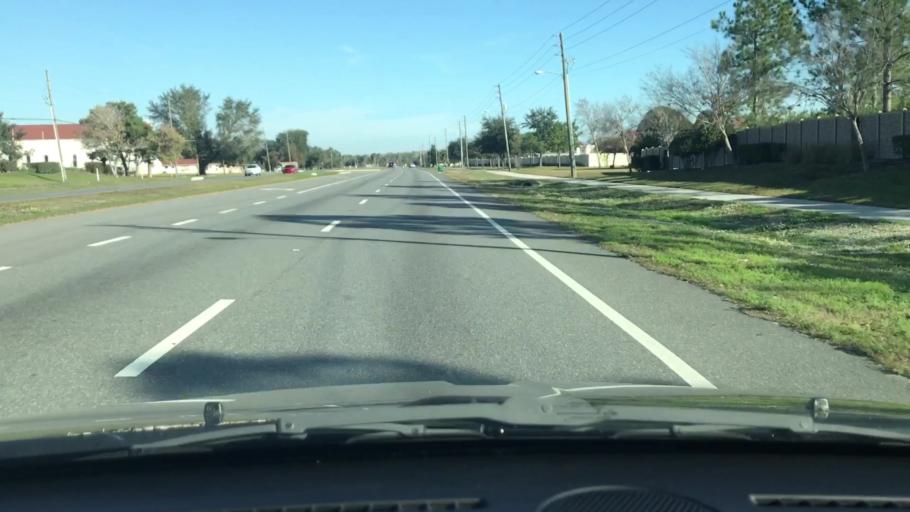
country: US
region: Florida
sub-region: Osceola County
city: Poinciana
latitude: 28.1756
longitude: -81.4400
